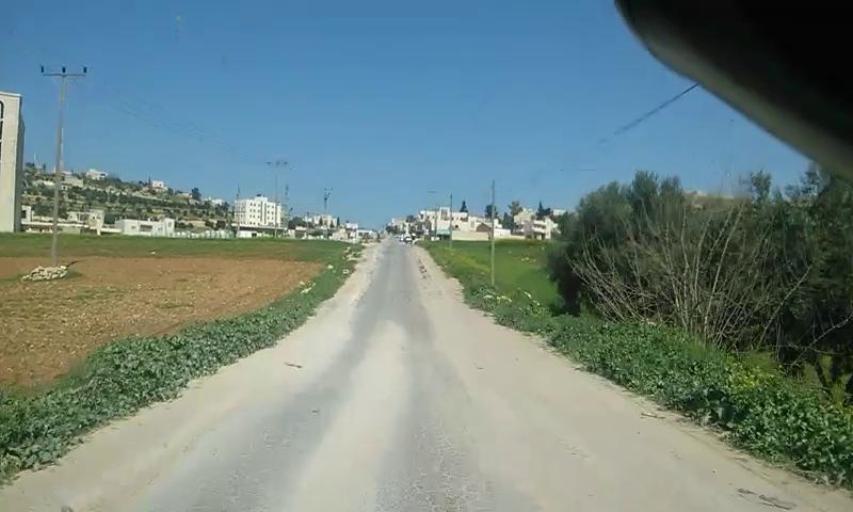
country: PS
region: West Bank
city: Bayt `Awwa
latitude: 31.5001
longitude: 34.9632
